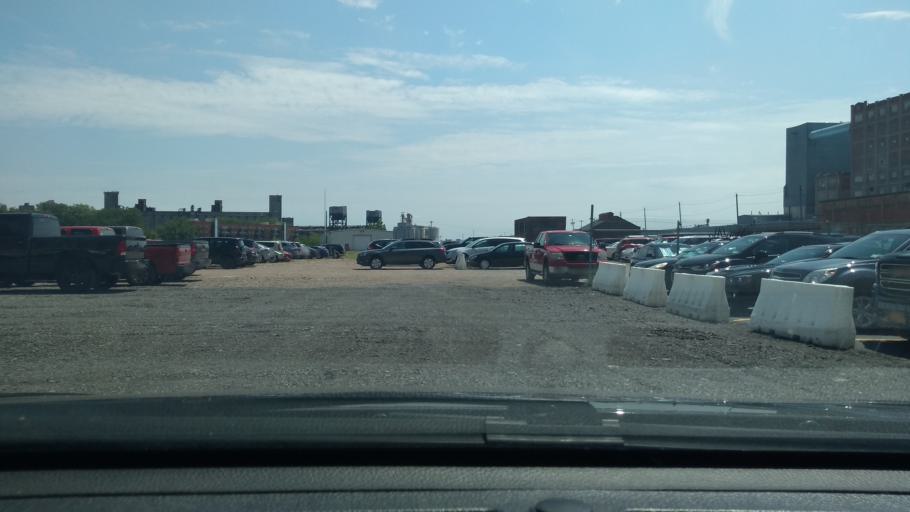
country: US
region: New York
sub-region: Erie County
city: Buffalo
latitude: 42.8684
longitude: -78.8719
